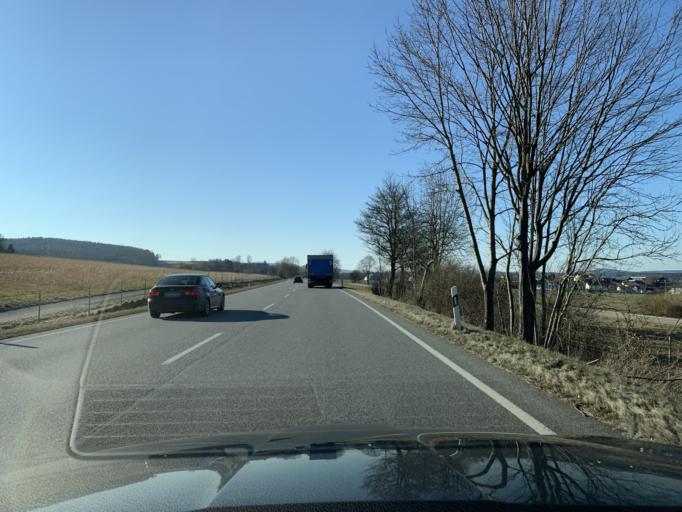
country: DE
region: Bavaria
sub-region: Upper Palatinate
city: Schonthal
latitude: 49.3307
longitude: 12.6245
